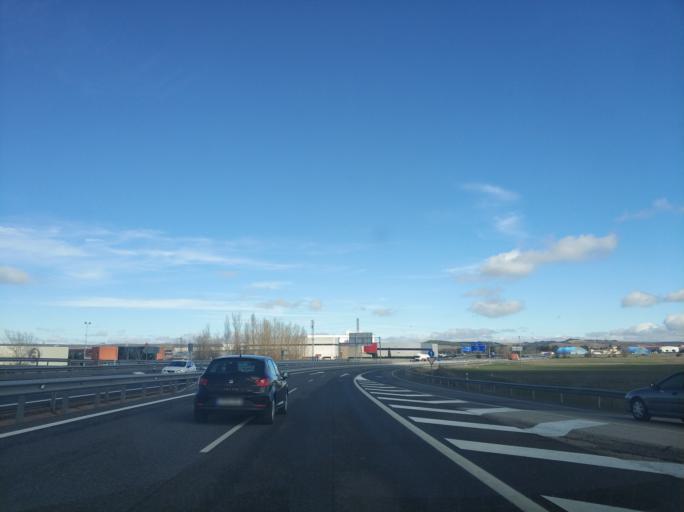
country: ES
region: Castille and Leon
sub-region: Provincia de Burgos
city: Cardenajimeno
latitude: 42.3466
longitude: -3.6383
